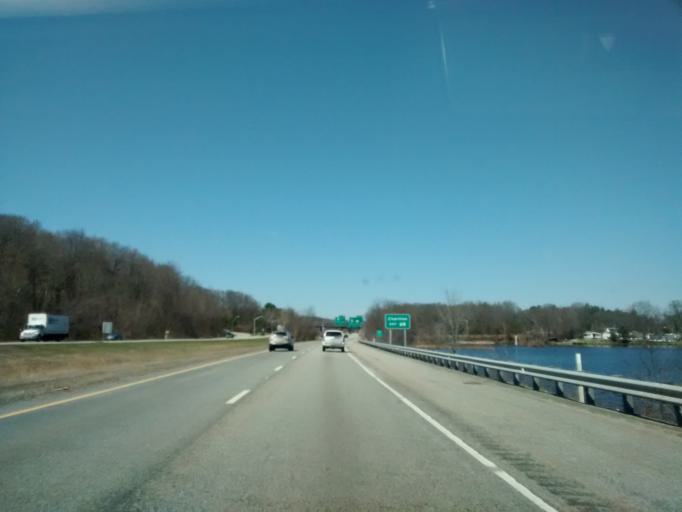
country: US
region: Massachusetts
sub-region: Worcester County
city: Auburn
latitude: 42.1789
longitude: -71.8457
